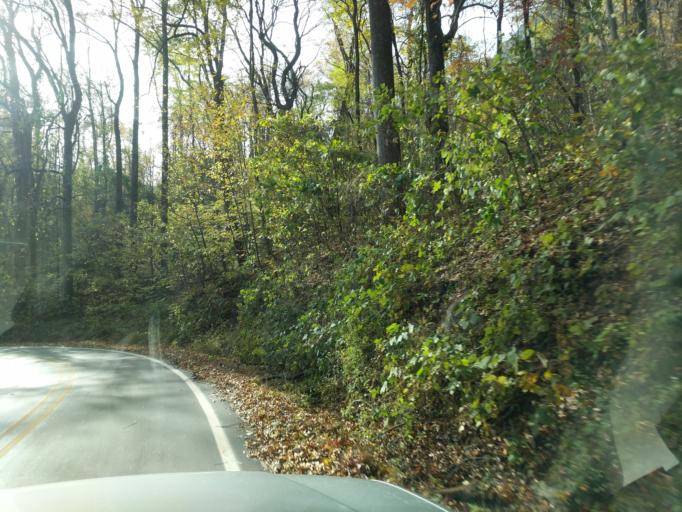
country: US
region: North Carolina
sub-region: Polk County
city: Columbus
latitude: 35.2639
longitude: -82.2356
